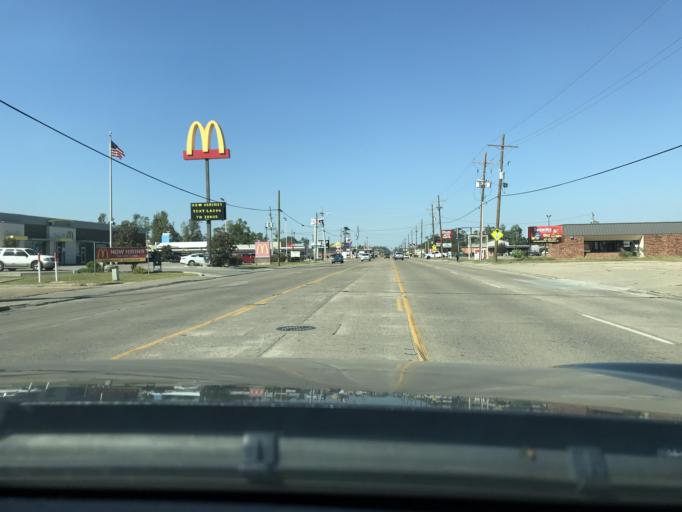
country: US
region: Louisiana
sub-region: Calcasieu Parish
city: Westlake
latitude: 30.2533
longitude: -93.2580
